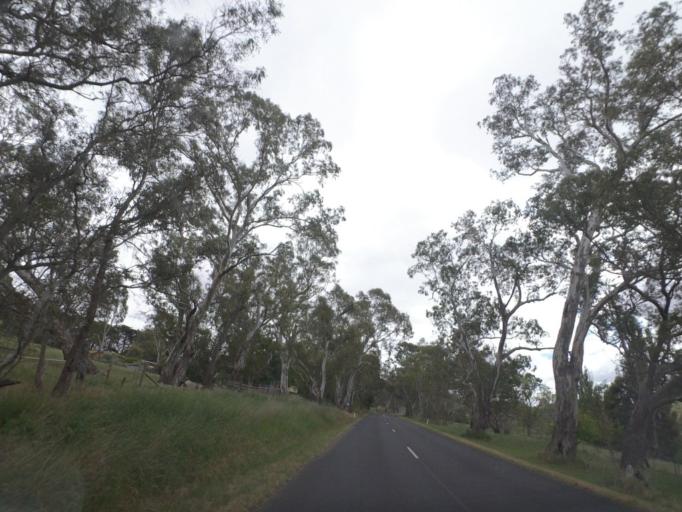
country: AU
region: Victoria
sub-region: Whittlesea
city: Whittlesea
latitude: -37.1963
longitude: 145.0381
